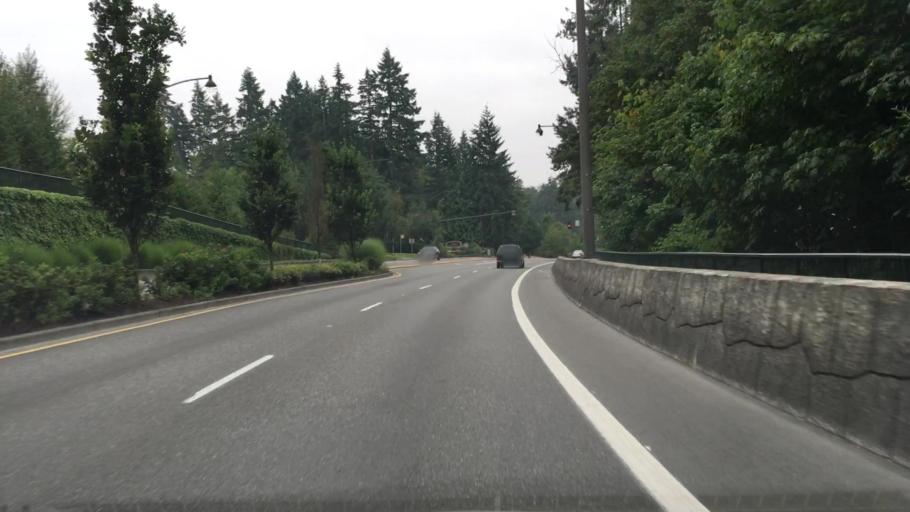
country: US
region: Washington
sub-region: King County
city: Newcastle
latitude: 47.5216
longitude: -122.1595
